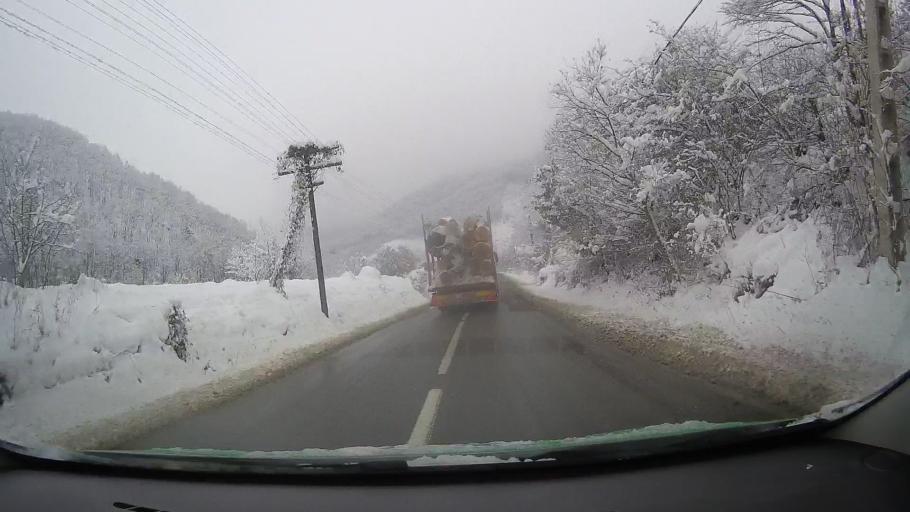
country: RO
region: Sibiu
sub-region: Comuna Orlat
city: Orlat
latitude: 45.7633
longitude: 23.9408
